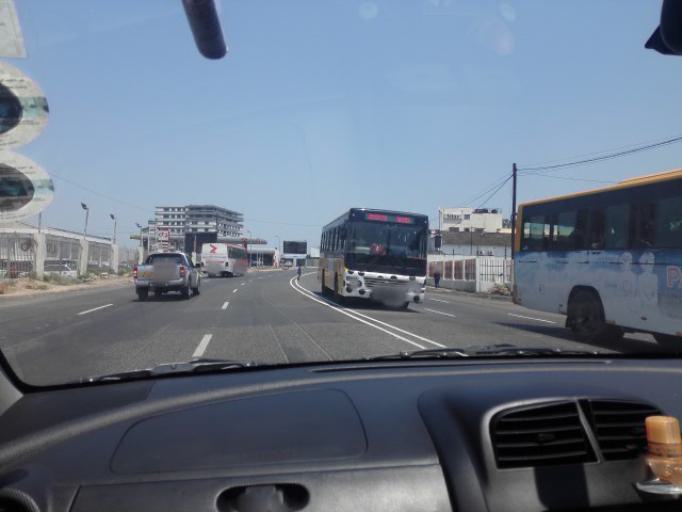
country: MZ
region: Maputo City
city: Maputo
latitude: -25.9541
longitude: 32.5519
